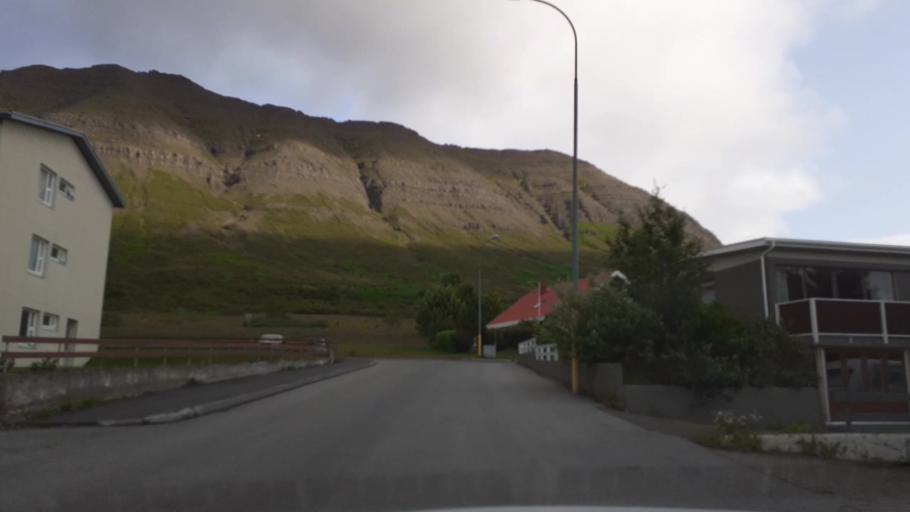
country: IS
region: East
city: Neskaupstadur
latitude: 65.1490
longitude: -13.6751
